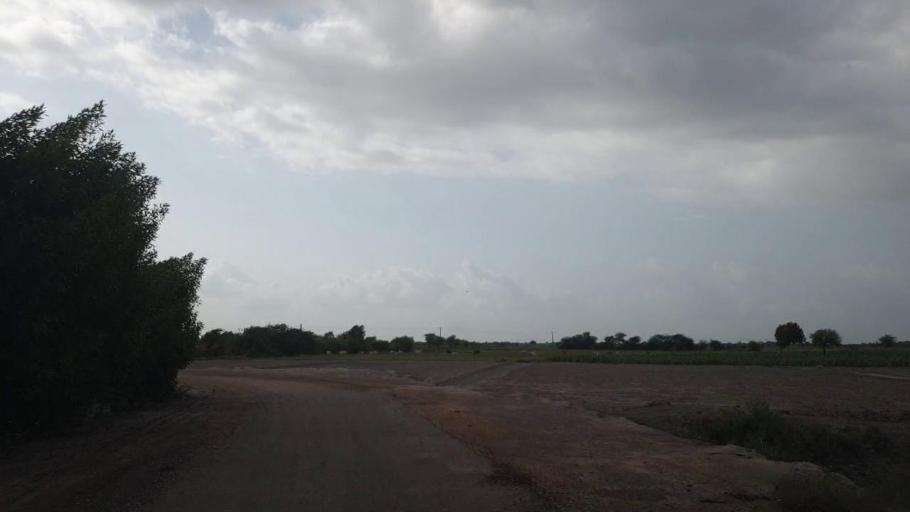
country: PK
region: Sindh
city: Kadhan
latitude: 24.5856
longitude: 69.0563
